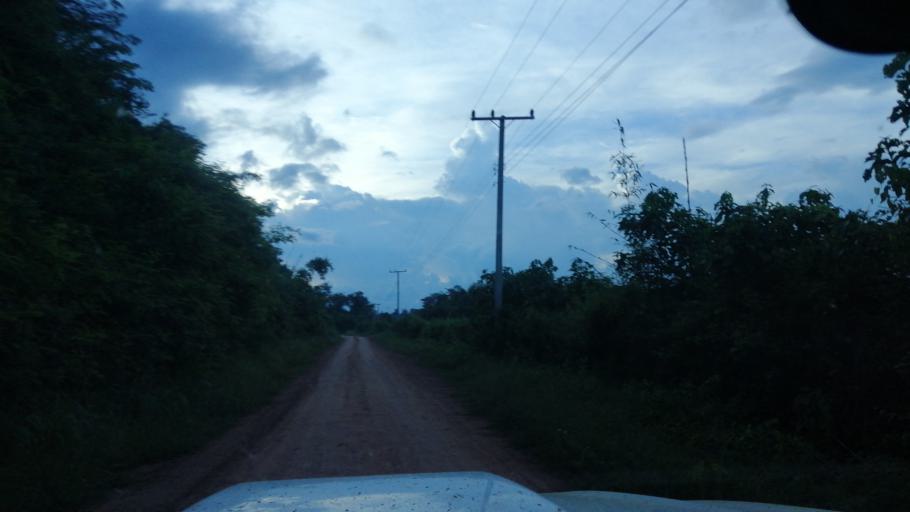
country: TH
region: Uttaradit
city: Ban Khok
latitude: 17.8731
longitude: 101.0851
